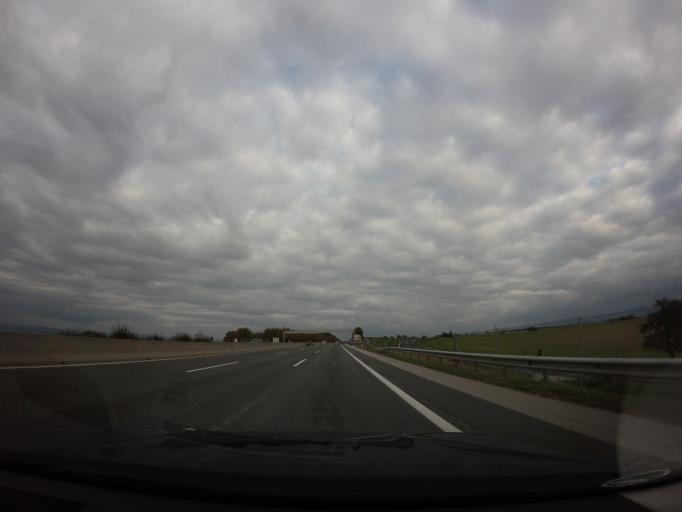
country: AT
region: Lower Austria
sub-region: Politischer Bezirk Amstetten
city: Wolfsbach
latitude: 48.1158
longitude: 14.7134
